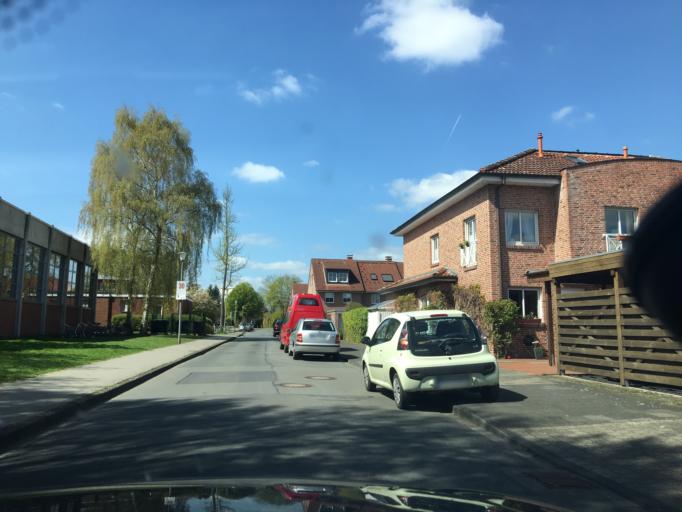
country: DE
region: North Rhine-Westphalia
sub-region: Regierungsbezirk Munster
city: Muenster
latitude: 51.9748
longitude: 7.6451
